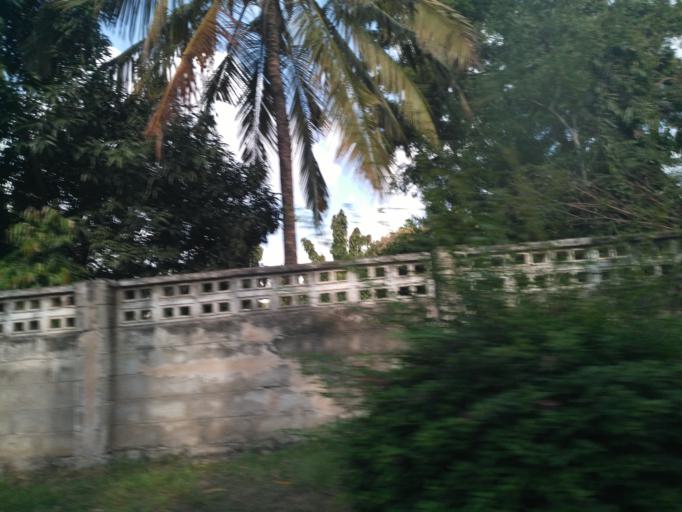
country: TZ
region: Dar es Salaam
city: Magomeni
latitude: -6.7477
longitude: 39.2359
